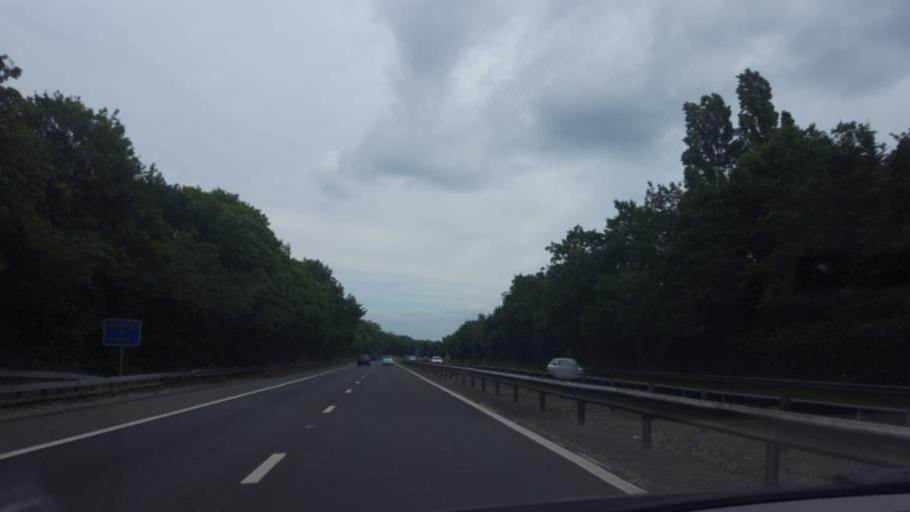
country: GB
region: England
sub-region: Royal Borough of Windsor and Maidenhead
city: Maidenhead
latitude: 51.5102
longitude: -0.7455
